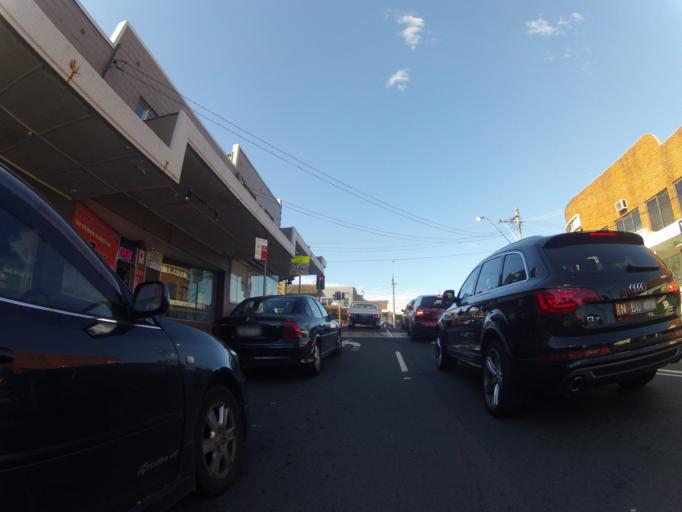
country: AU
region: New South Wales
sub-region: Hurstville
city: Penshurst
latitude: -33.9500
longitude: 151.0808
